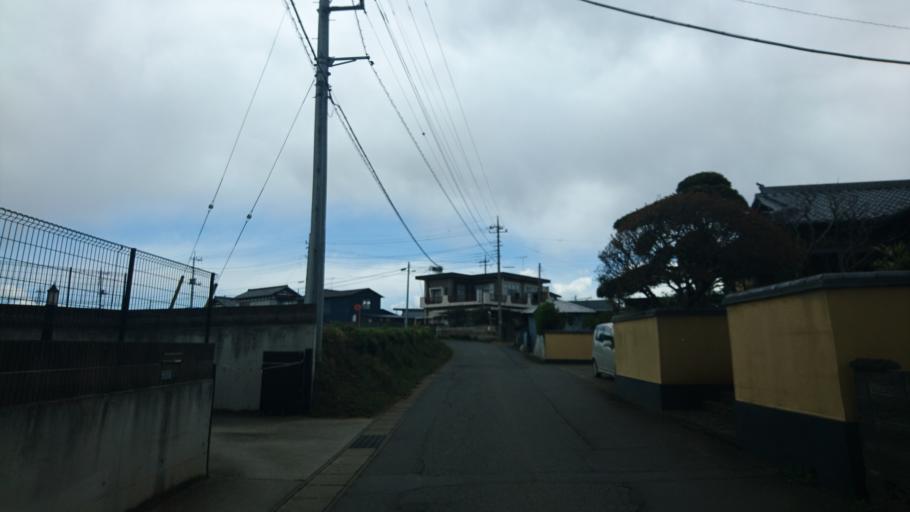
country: JP
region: Ibaraki
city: Yuki
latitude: 36.2746
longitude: 139.9077
